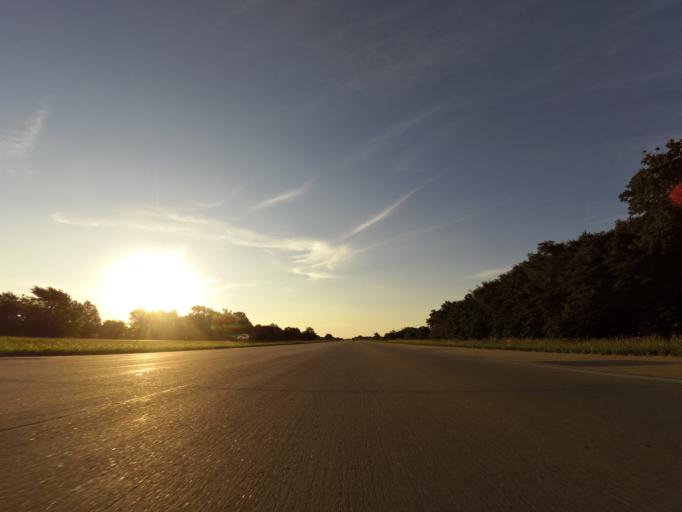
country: US
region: Kansas
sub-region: Reno County
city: Haven
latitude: 37.8855
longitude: -97.7339
